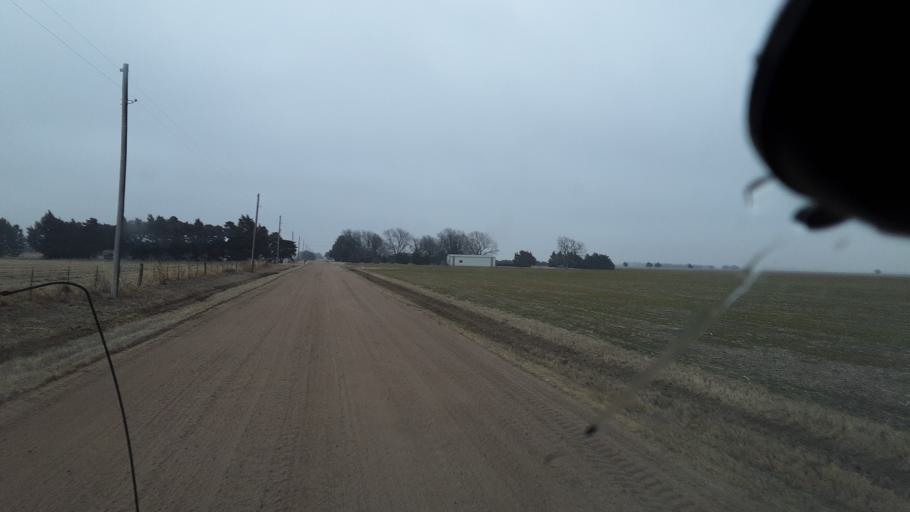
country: US
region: Kansas
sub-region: Reno County
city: South Hutchinson
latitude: 37.9846
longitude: -98.0065
